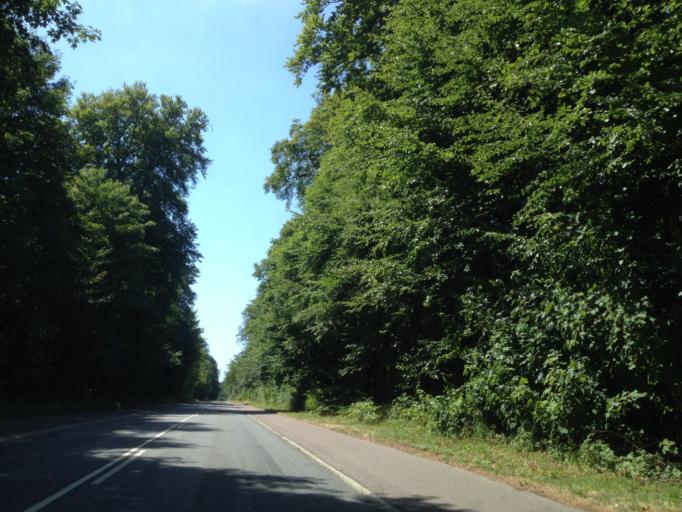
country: DK
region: Capital Region
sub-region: Rudersdal Kommune
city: Trorod
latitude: 55.8215
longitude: 12.5602
